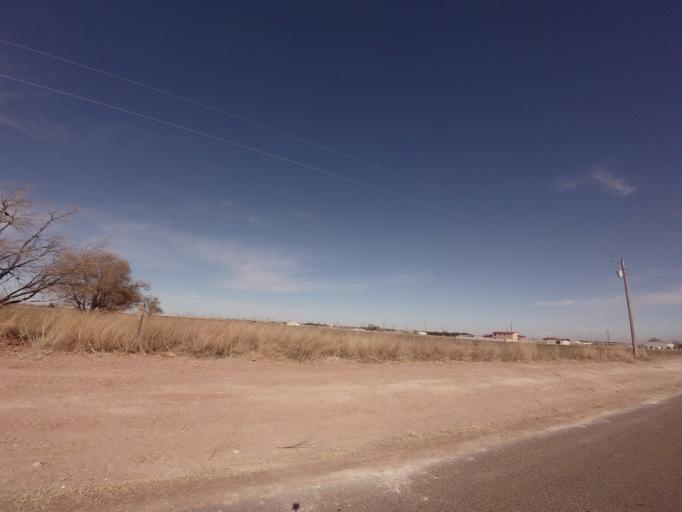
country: US
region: New Mexico
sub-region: Curry County
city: Clovis
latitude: 34.4049
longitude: -103.1493
